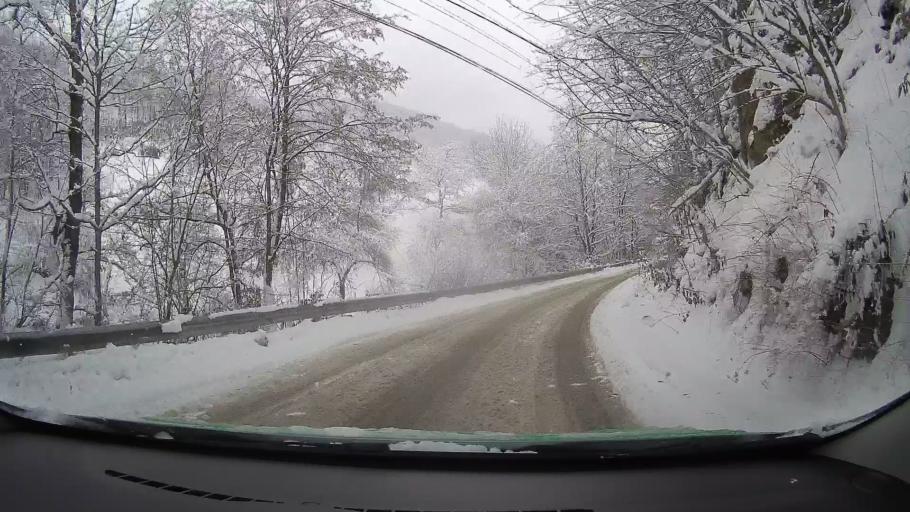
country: RO
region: Alba
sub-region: Comuna Sugag
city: Dobra
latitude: 45.7633
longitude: 23.6552
